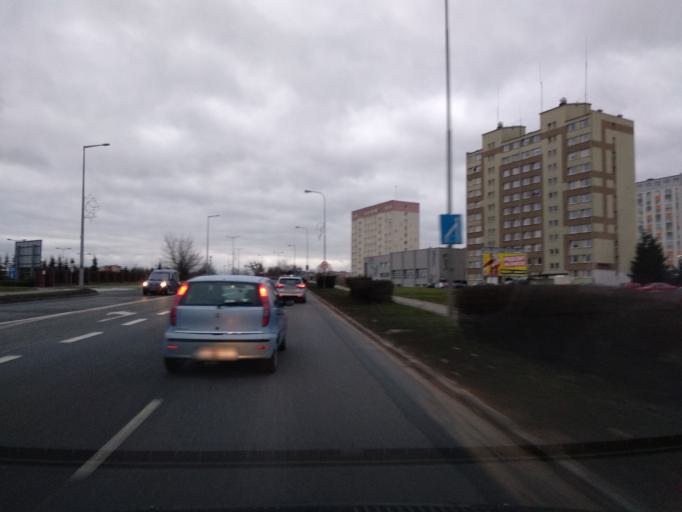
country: PL
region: Greater Poland Voivodeship
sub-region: Konin
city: Konin
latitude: 52.2334
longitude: 18.2681
